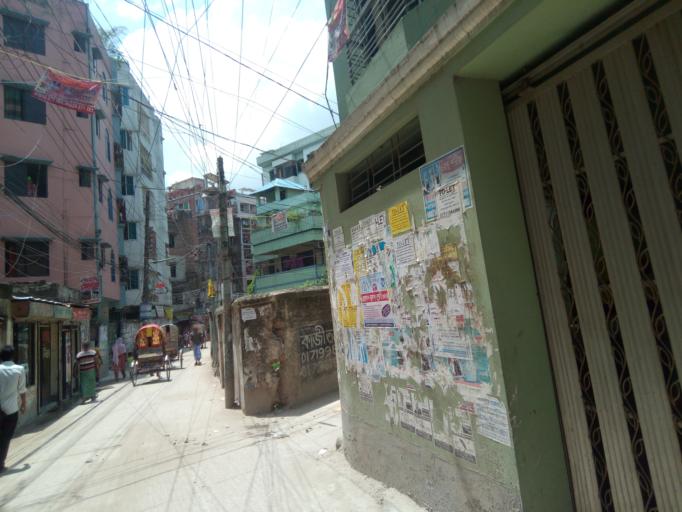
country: BD
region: Dhaka
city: Azimpur
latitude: 23.7632
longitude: 90.3916
